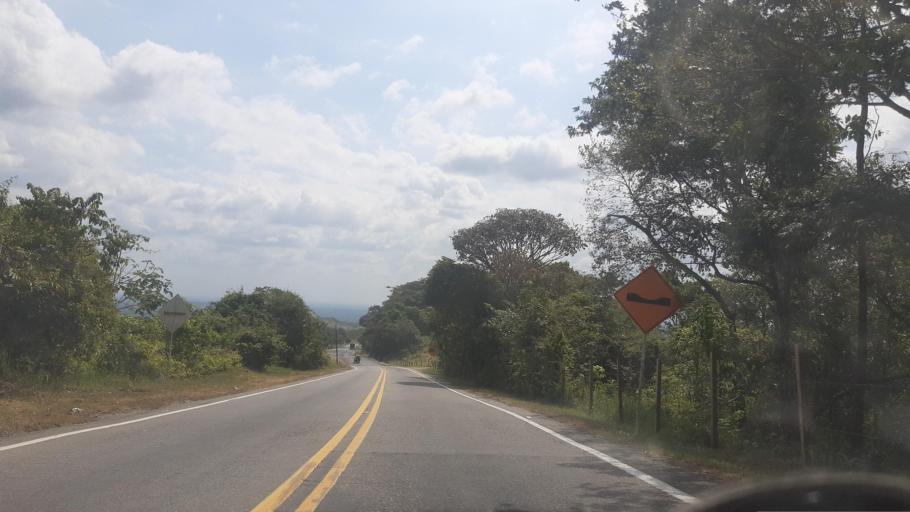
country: CO
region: Casanare
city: Monterrey
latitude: 4.8451
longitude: -72.8436
